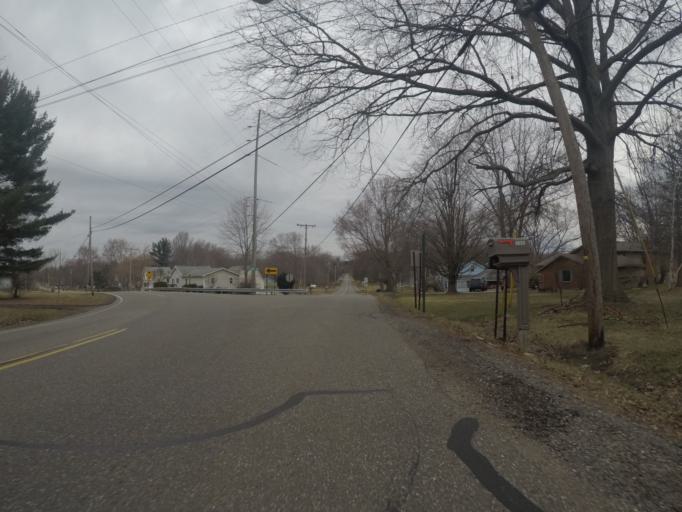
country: US
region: Ohio
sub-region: Portage County
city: Ravenna
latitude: 41.1649
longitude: -81.2803
